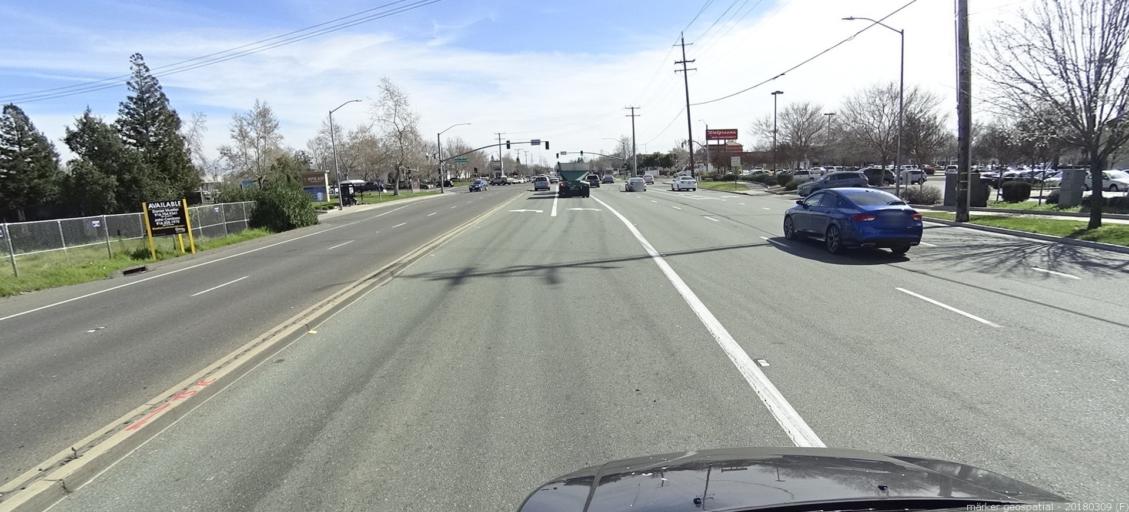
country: US
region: California
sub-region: Sacramento County
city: Vineyard
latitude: 38.4526
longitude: -121.3731
